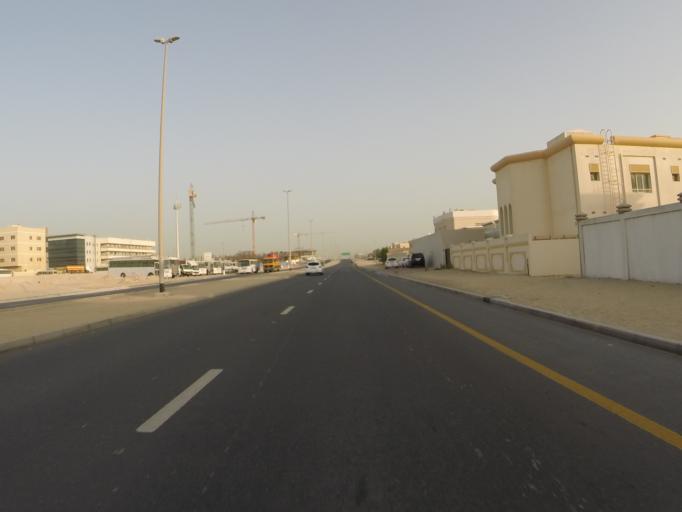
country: AE
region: Dubai
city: Dubai
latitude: 25.1597
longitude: 55.2526
